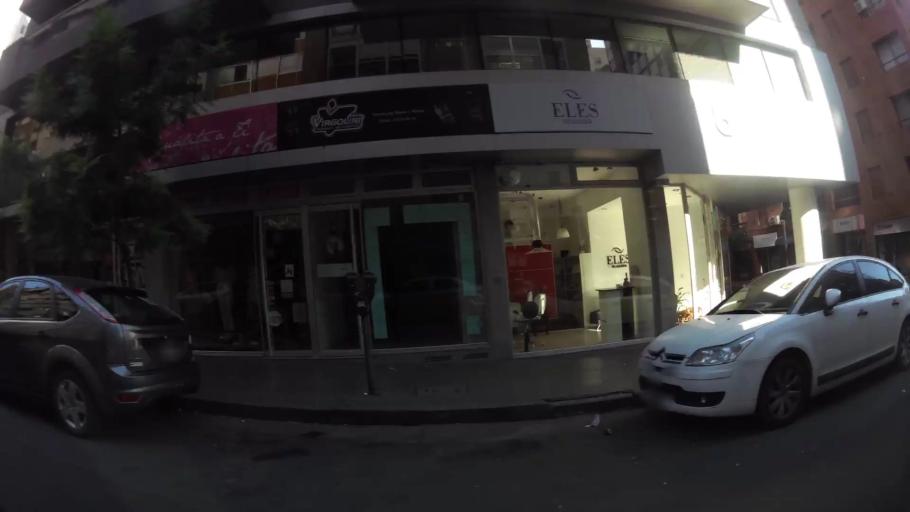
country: AR
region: Cordoba
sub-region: Departamento de Capital
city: Cordoba
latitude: -31.4218
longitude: -64.1865
